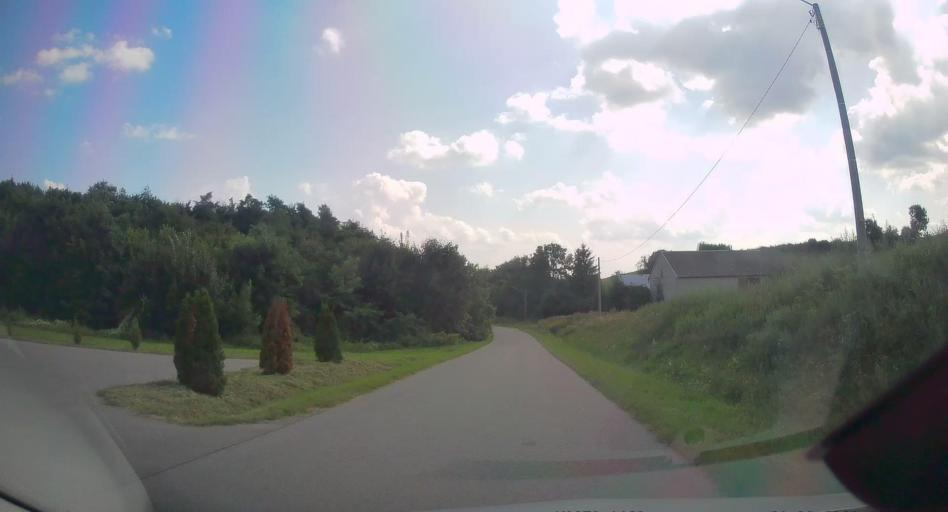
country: PL
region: Lesser Poland Voivodeship
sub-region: Powiat bochenski
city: Dziewin
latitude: 50.1520
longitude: 20.4636
